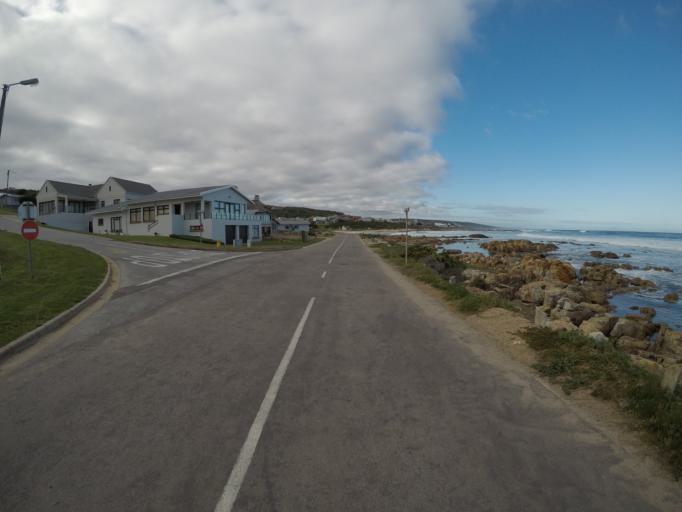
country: ZA
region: Western Cape
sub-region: Eden District Municipality
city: Riversdale
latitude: -34.4283
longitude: 21.3364
